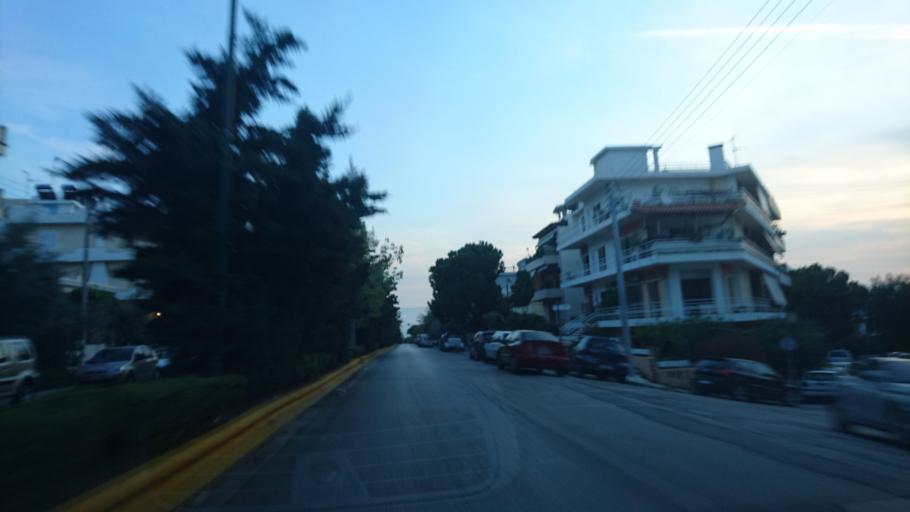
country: GR
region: Attica
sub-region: Nomarchia Athinas
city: Ilioupoli
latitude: 37.9300
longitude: 23.7548
